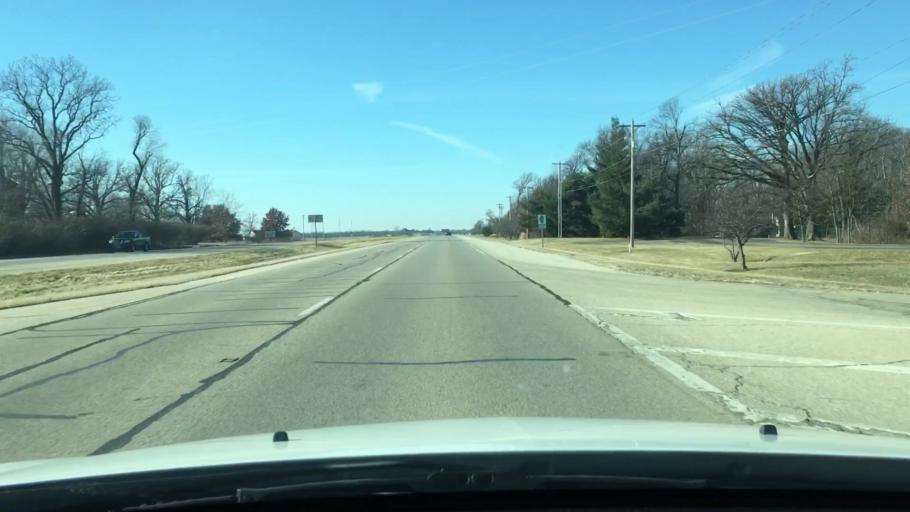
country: US
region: Illinois
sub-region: Woodford County
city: Metamora
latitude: 40.7793
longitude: -89.4091
